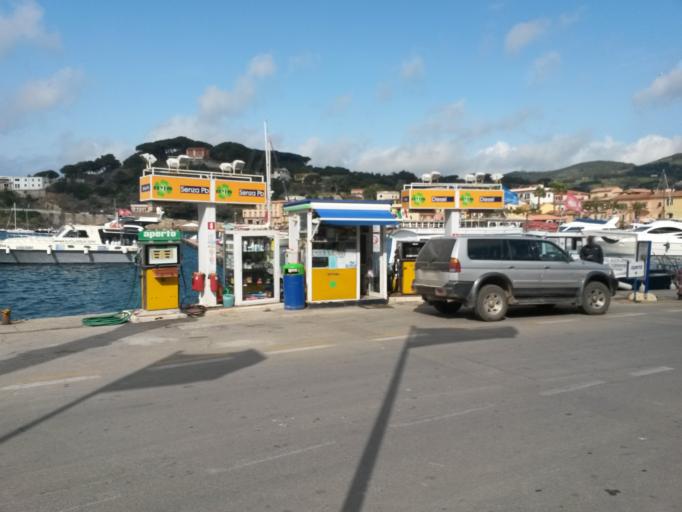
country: IT
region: Tuscany
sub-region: Provincia di Livorno
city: Porto Azzurro
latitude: 42.7646
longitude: 10.3986
